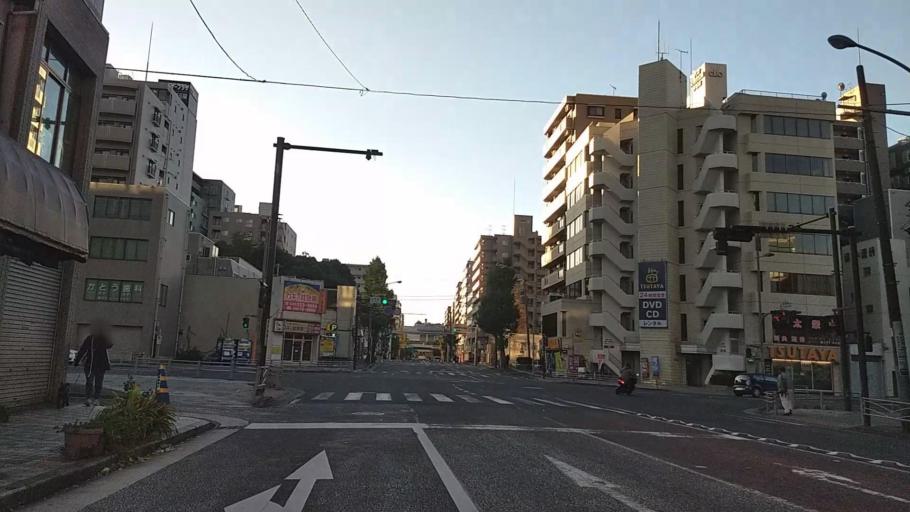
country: JP
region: Kanagawa
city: Yokohama
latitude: 35.4383
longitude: 139.6247
